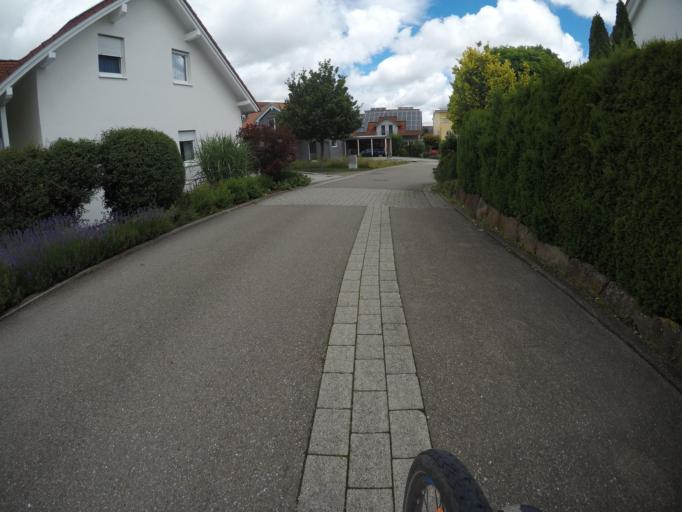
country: DE
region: Baden-Wuerttemberg
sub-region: Regierungsbezirk Stuttgart
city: Deckenpfronn
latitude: 48.6200
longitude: 8.8289
